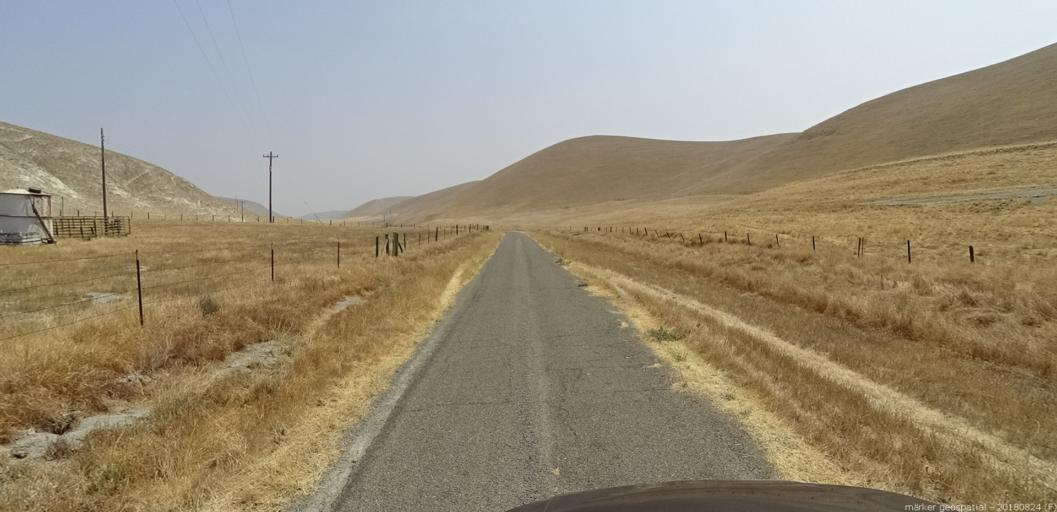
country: US
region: California
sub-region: Monterey County
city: King City
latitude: 36.1911
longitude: -120.9767
